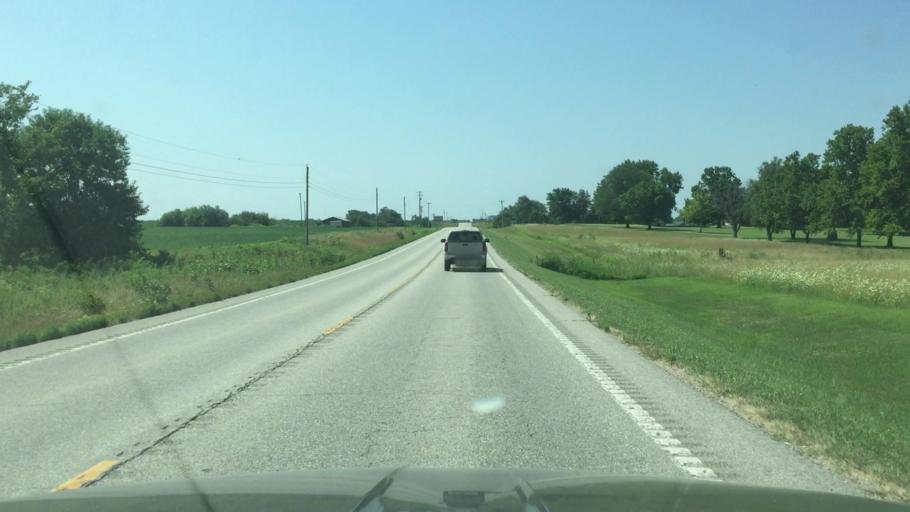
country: US
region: Missouri
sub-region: Morgan County
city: Versailles
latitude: 38.4670
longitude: -92.8089
